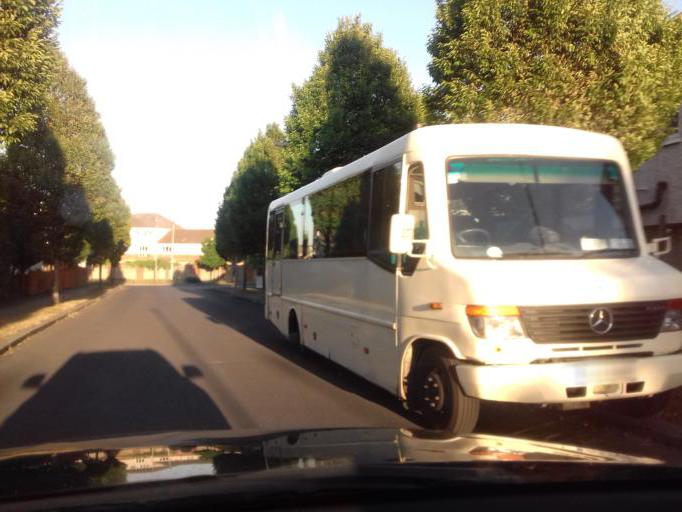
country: IE
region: Leinster
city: Hartstown
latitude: 53.4022
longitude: -6.4380
